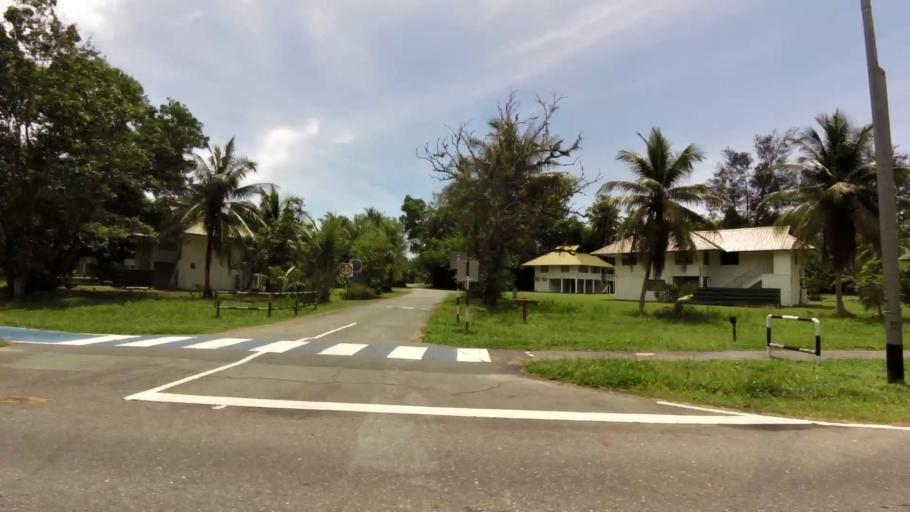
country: BN
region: Belait
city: Seria
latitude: 4.6034
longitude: 114.2851
